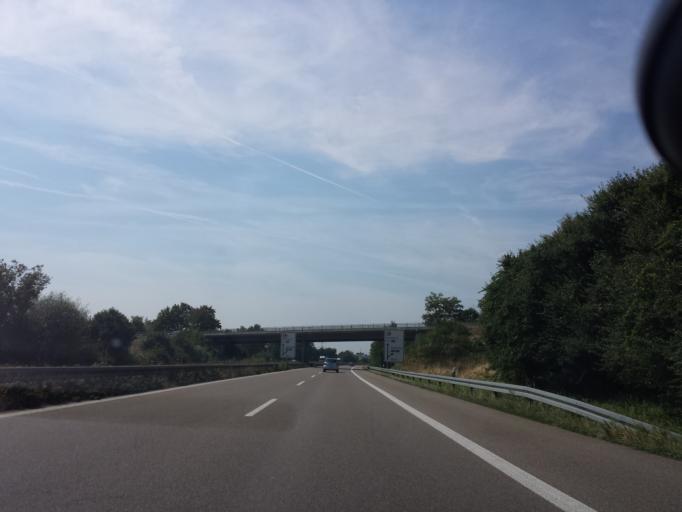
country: DE
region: Bavaria
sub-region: Swabia
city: Senden
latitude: 48.3320
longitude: 10.0543
